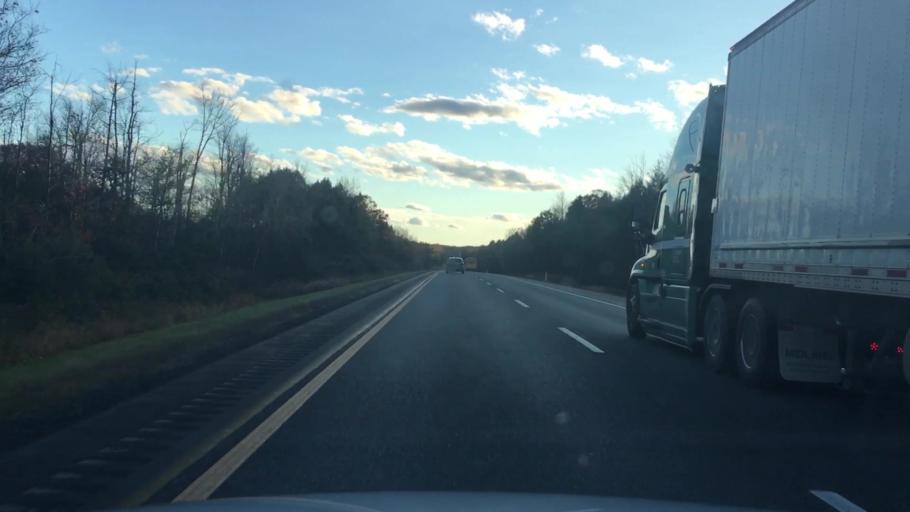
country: US
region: Maine
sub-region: Kennebec County
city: Sidney
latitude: 44.4182
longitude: -69.7434
